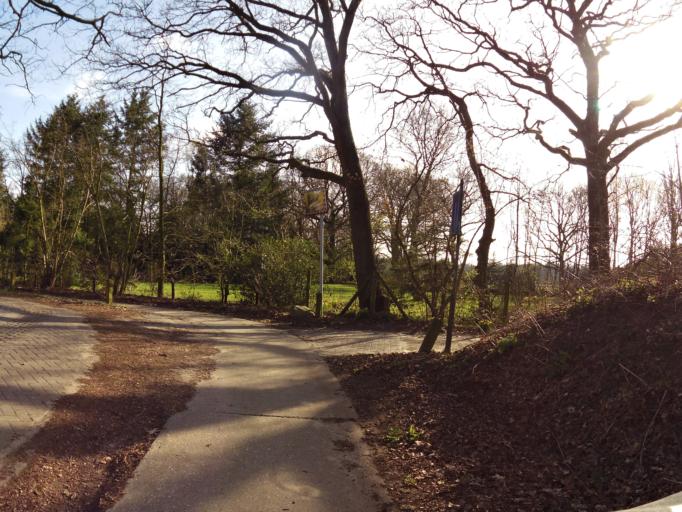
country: NL
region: Overijssel
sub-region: Gemeente Steenwijkerland
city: Steenwijk
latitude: 52.8031
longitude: 6.1170
